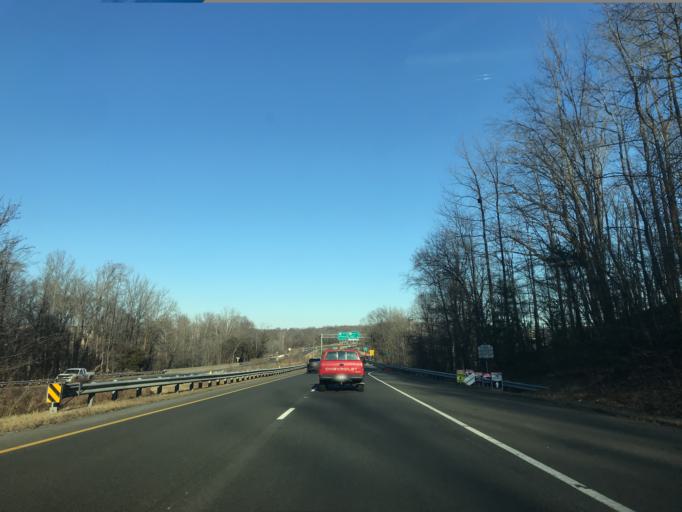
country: US
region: Maryland
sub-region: Prince George's County
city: Upper Marlboro
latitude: 38.8106
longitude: -76.7546
